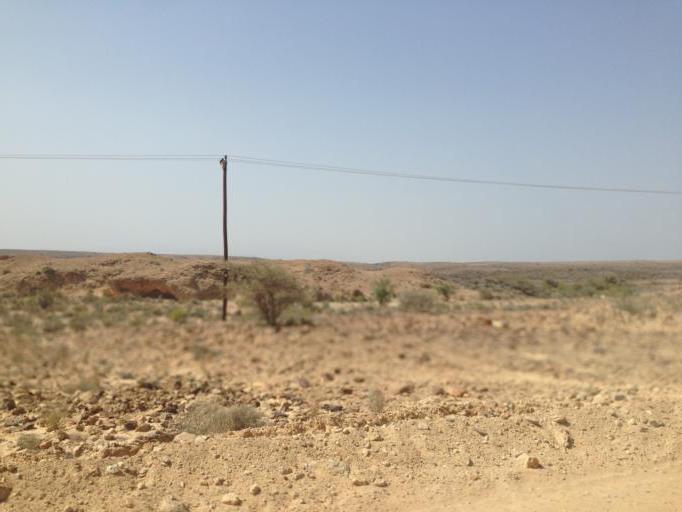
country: OM
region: Ash Sharqiyah
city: Ibra'
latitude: 23.0815
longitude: 58.9065
